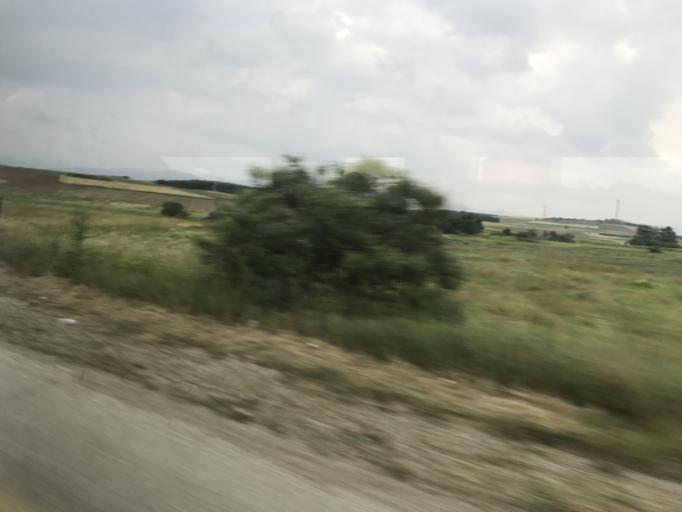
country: GR
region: East Macedonia and Thrace
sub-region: Nomos Rodopis
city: Arisvi
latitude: 41.0752
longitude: 25.5845
